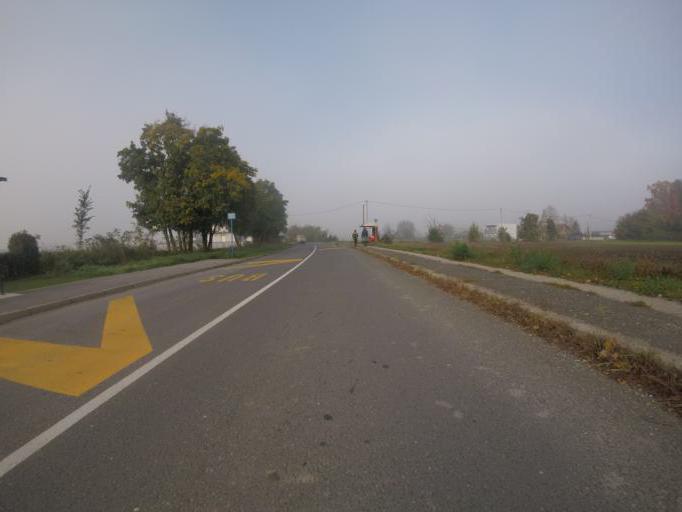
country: HR
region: Zagrebacka
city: Micevec
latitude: 45.7641
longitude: 16.0780
